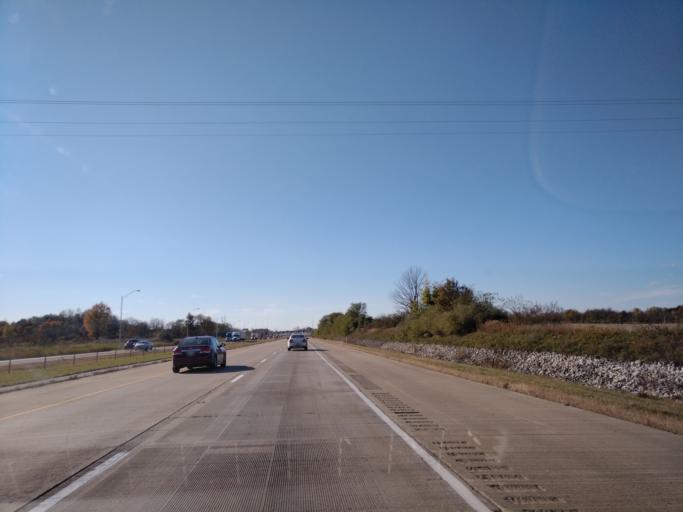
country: US
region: Indiana
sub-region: Marion County
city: Cumberland
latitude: 39.8196
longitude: -85.8972
